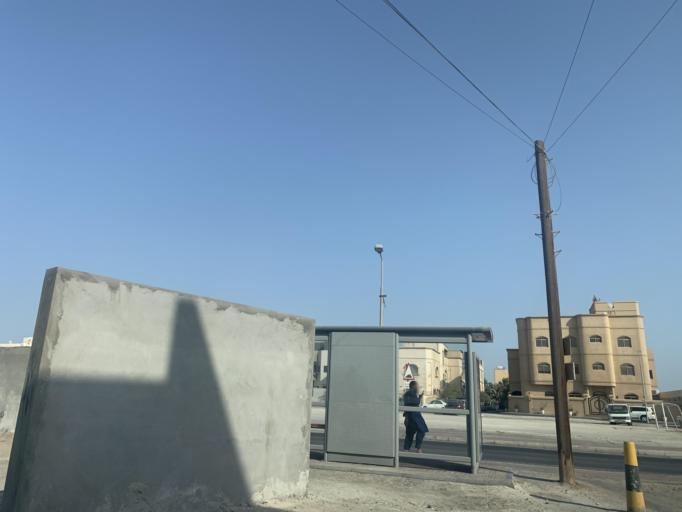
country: BH
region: Muharraq
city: Al Muharraq
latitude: 26.2812
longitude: 50.6299
